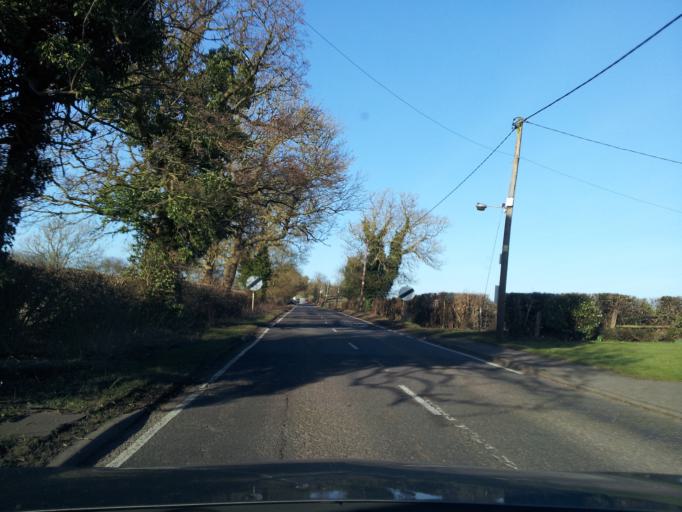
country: GB
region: England
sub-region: Northamptonshire
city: Bugbrooke
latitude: 52.2380
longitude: -0.9744
